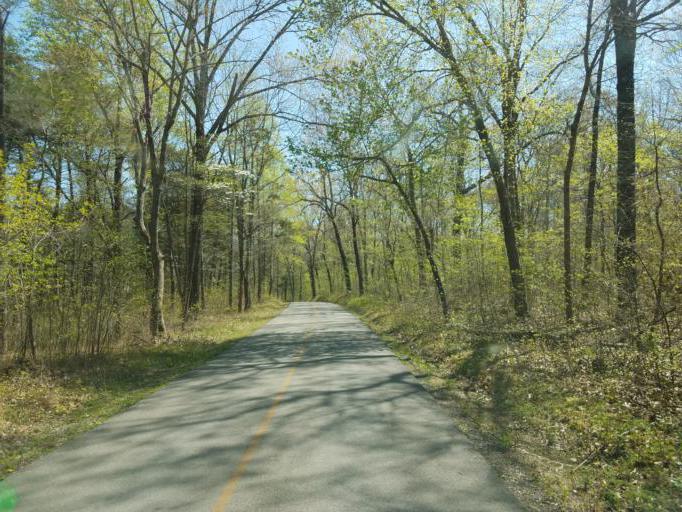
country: US
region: Kentucky
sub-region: Barren County
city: Cave City
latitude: 37.1959
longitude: -86.0535
